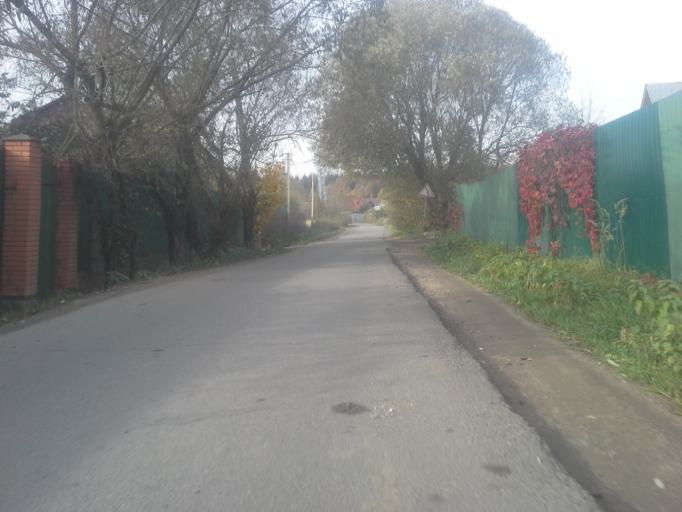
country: RU
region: Moskovskaya
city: Aprelevka
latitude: 55.5567
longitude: 37.0555
